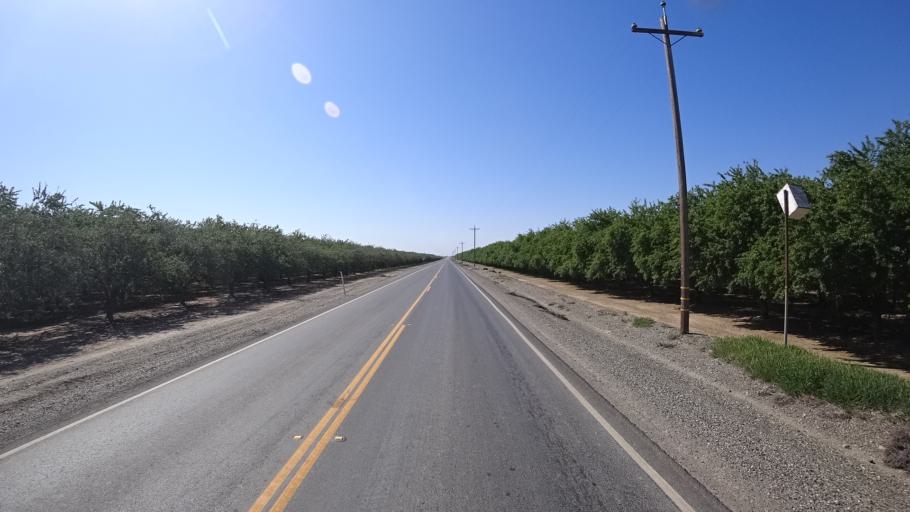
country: US
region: California
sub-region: Glenn County
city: Hamilton City
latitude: 39.6583
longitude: -122.0650
